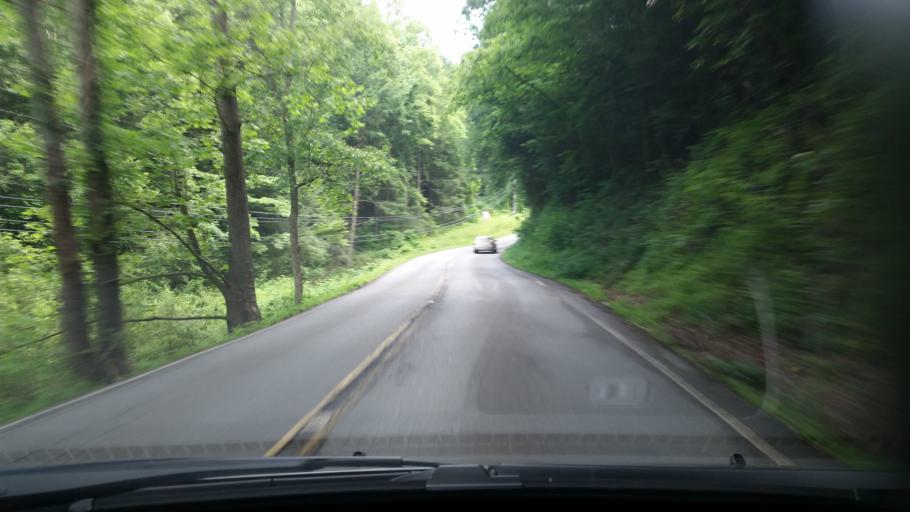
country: US
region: Tennessee
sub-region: Sevier County
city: Gatlinburg
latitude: 35.7379
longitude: -83.4666
